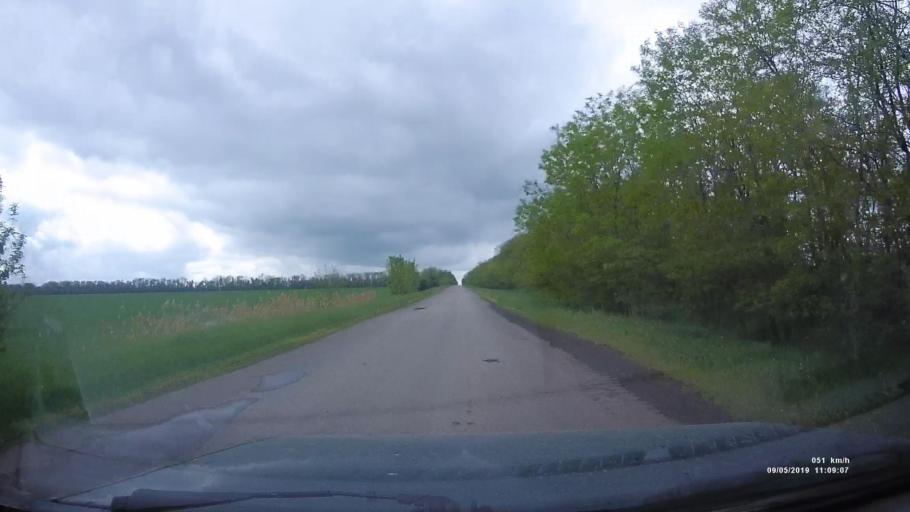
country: RU
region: Krasnodarskiy
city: Kanelovskaya
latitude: 46.7858
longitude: 39.2118
